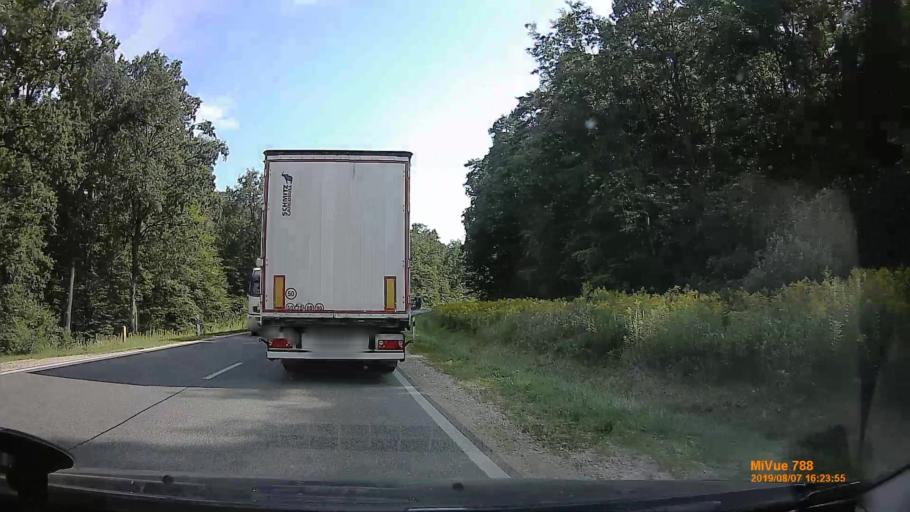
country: HU
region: Zala
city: Zalalovo
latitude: 46.7424
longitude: 16.5547
